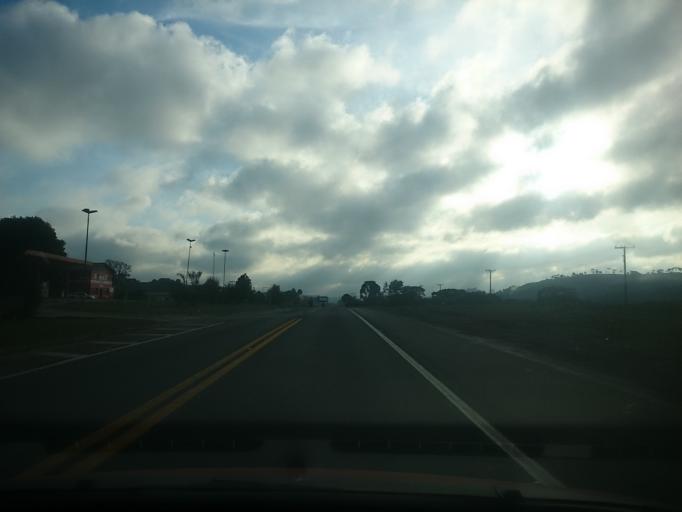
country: BR
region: Santa Catarina
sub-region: Lages
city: Lages
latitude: -28.0104
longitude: -50.5455
